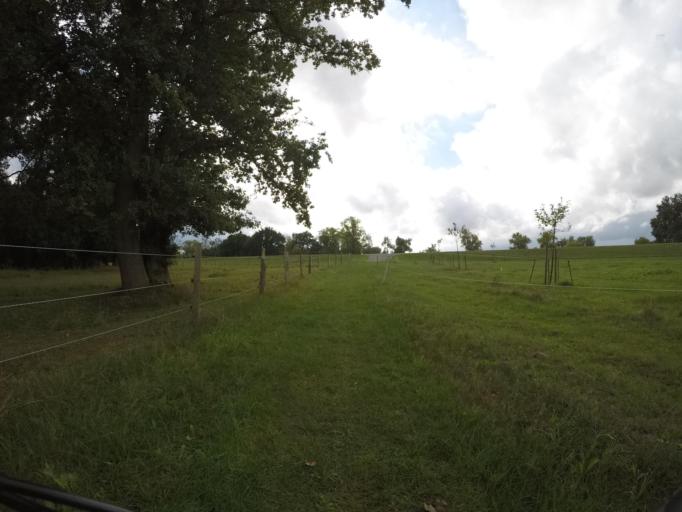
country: DE
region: Lower Saxony
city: Neu Darchau
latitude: 53.2471
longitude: 10.8779
